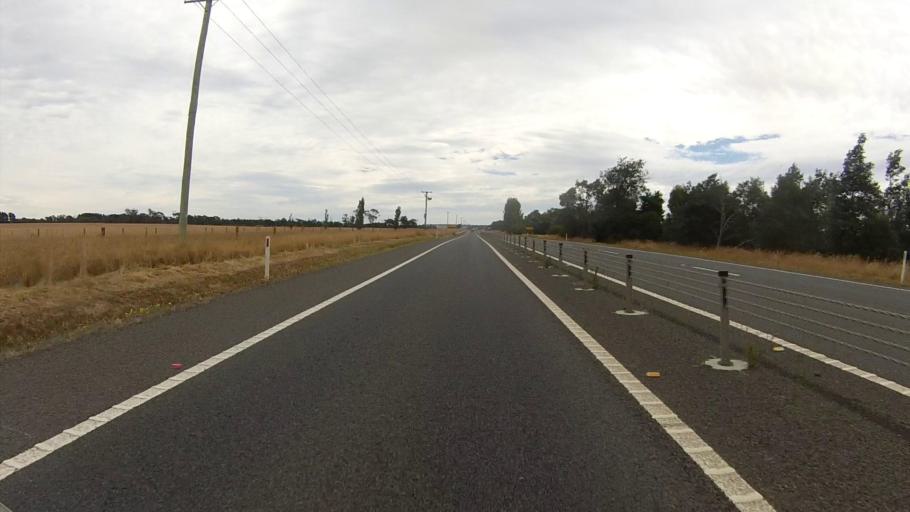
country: AU
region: Tasmania
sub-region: Northern Midlands
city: Evandale
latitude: -41.6432
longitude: 147.2356
